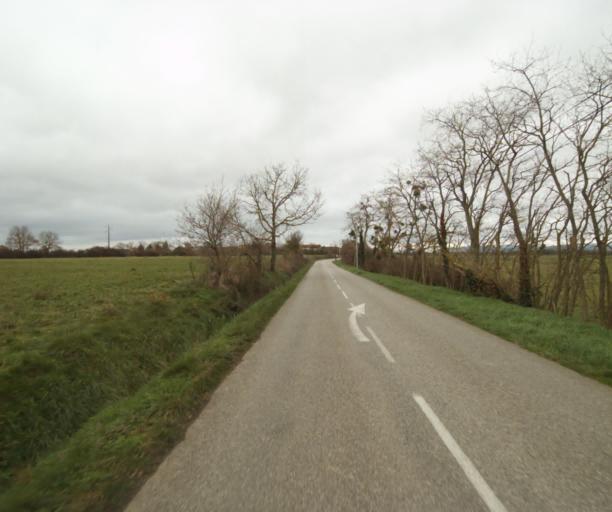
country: FR
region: Midi-Pyrenees
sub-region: Departement de l'Ariege
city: Mazeres
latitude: 43.1871
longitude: 1.6342
